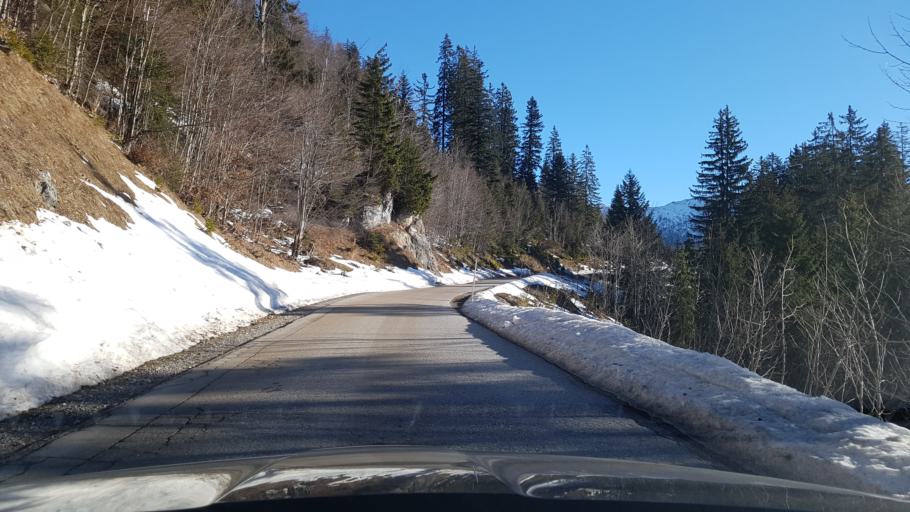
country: AT
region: Salzburg
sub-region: Politischer Bezirk Hallein
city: Abtenau
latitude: 47.6208
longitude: 13.4040
